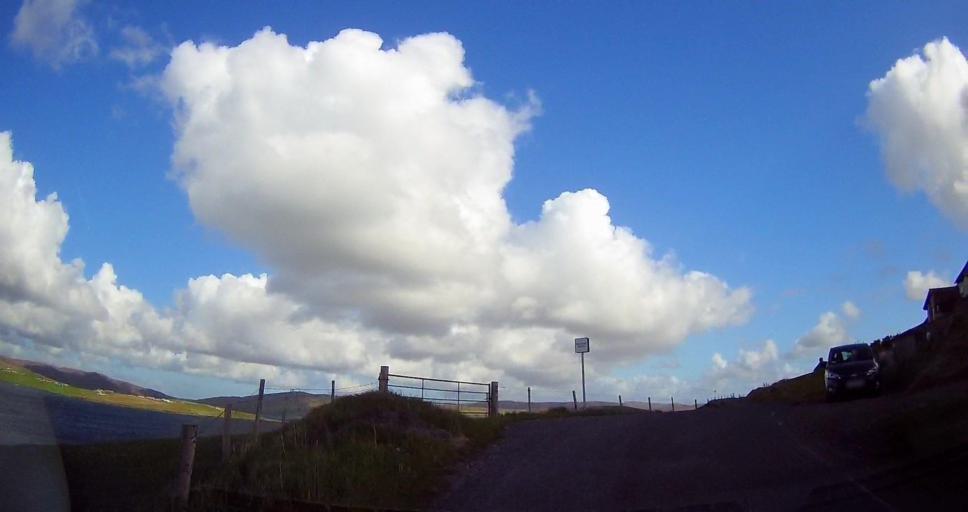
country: GB
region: Scotland
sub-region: Shetland Islands
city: Lerwick
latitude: 60.3751
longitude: -1.3834
